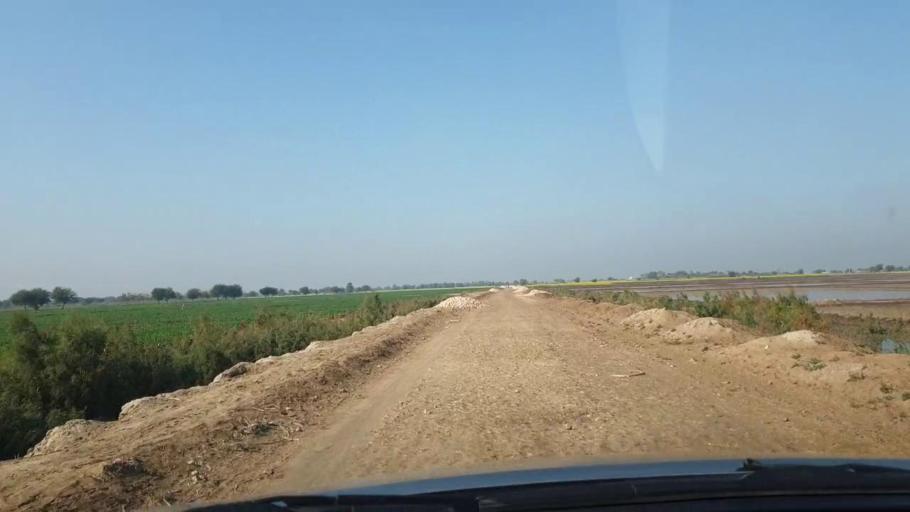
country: PK
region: Sindh
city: Berani
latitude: 25.8291
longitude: 68.9265
